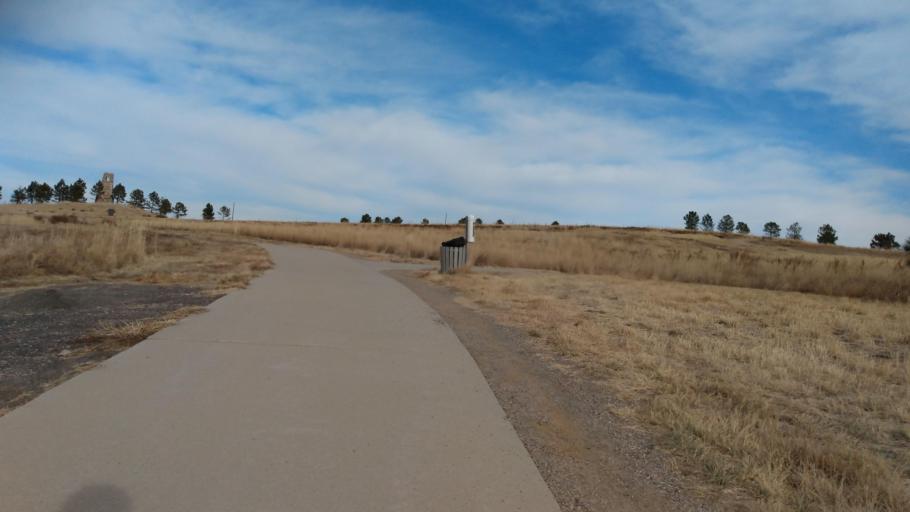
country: US
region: Colorado
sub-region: Boulder County
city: Lafayette
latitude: 39.9980
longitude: -105.0520
